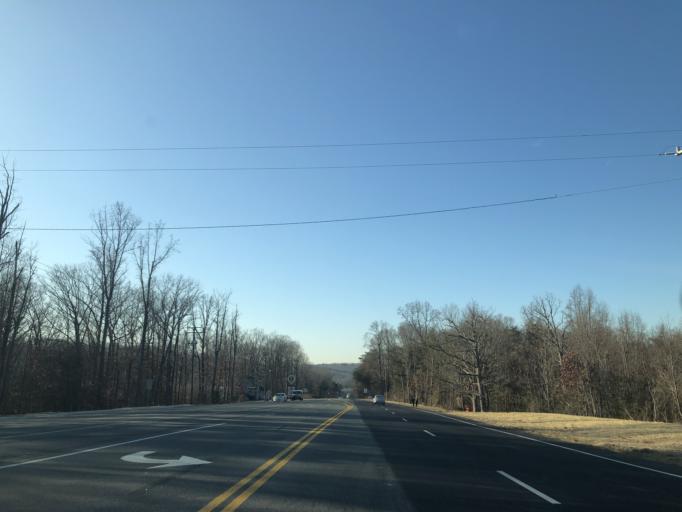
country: US
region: Virginia
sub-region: Stafford County
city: Stafford
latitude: 38.4138
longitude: -77.4109
